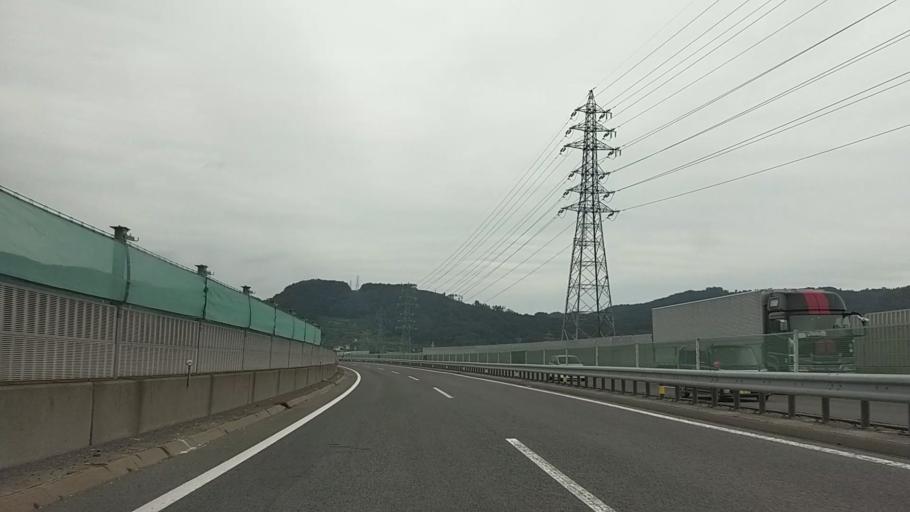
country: JP
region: Nagano
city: Nagano-shi
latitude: 36.5578
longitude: 138.1190
